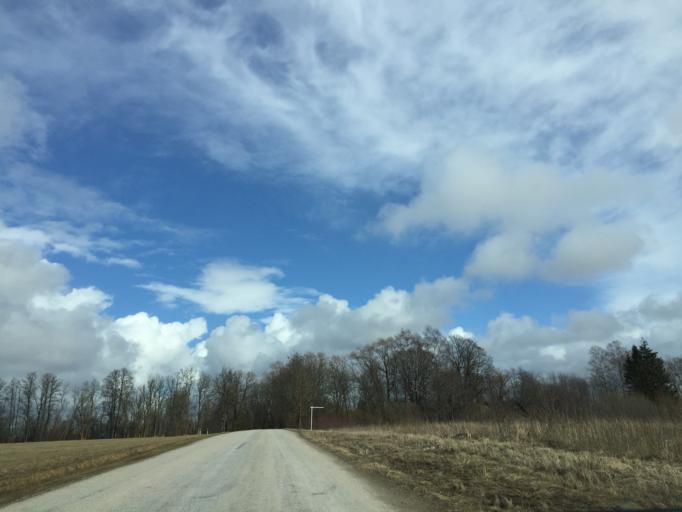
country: EE
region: Laeaene
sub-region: Lihula vald
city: Lihula
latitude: 58.7350
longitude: 23.8283
